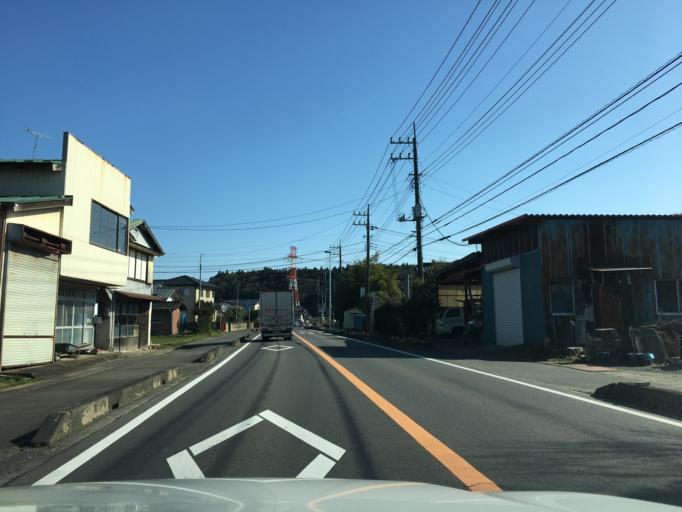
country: JP
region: Ibaraki
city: Omiya
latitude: 36.4915
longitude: 140.3752
